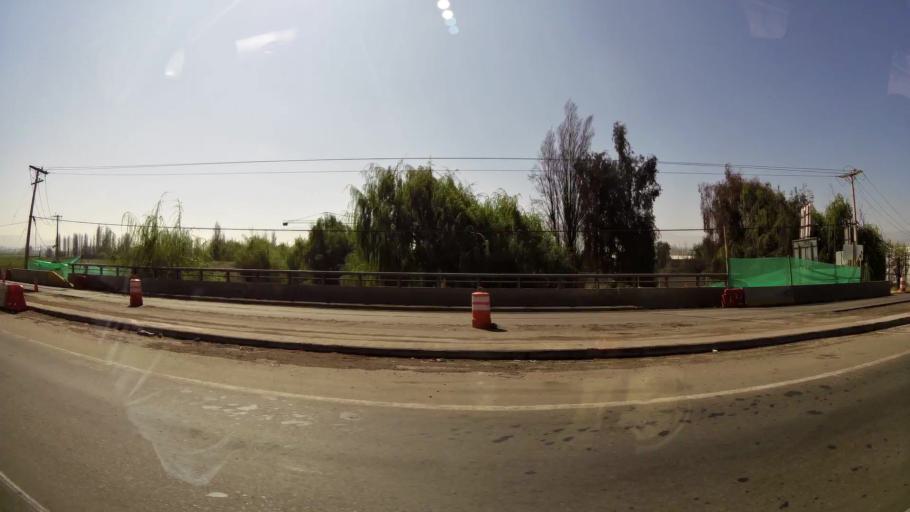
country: CL
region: Santiago Metropolitan
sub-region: Provincia de Chacabuco
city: Chicureo Abajo
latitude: -33.2695
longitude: -70.7435
